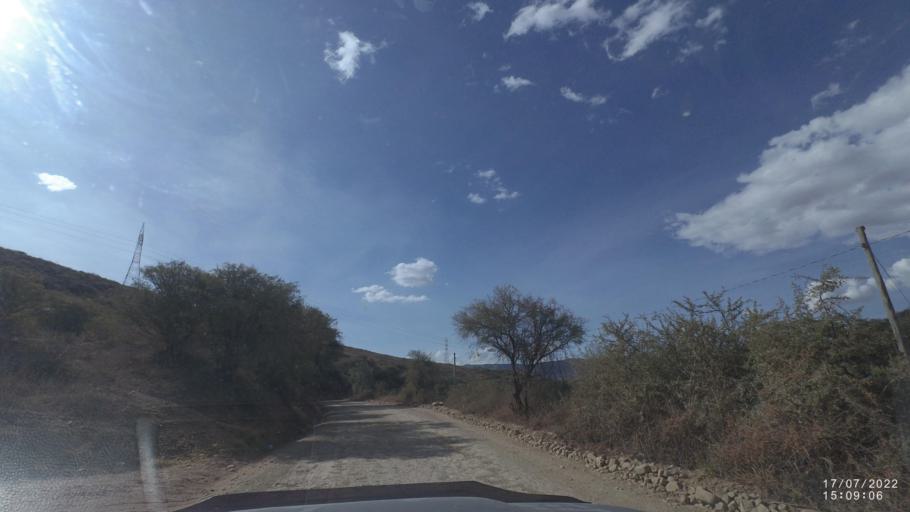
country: BO
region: Cochabamba
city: Capinota
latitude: -17.5760
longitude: -66.2665
